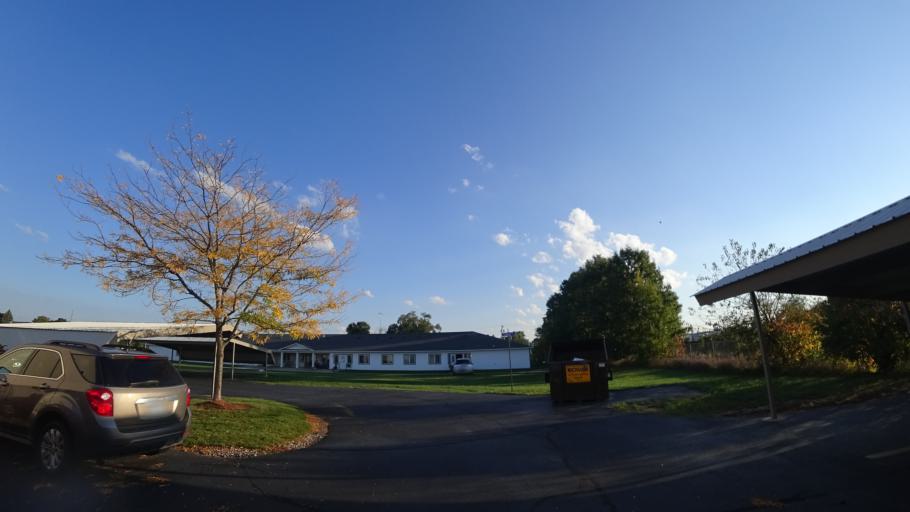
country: US
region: Michigan
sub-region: Saint Joseph County
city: Three Rivers
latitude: 41.9442
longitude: -85.6480
